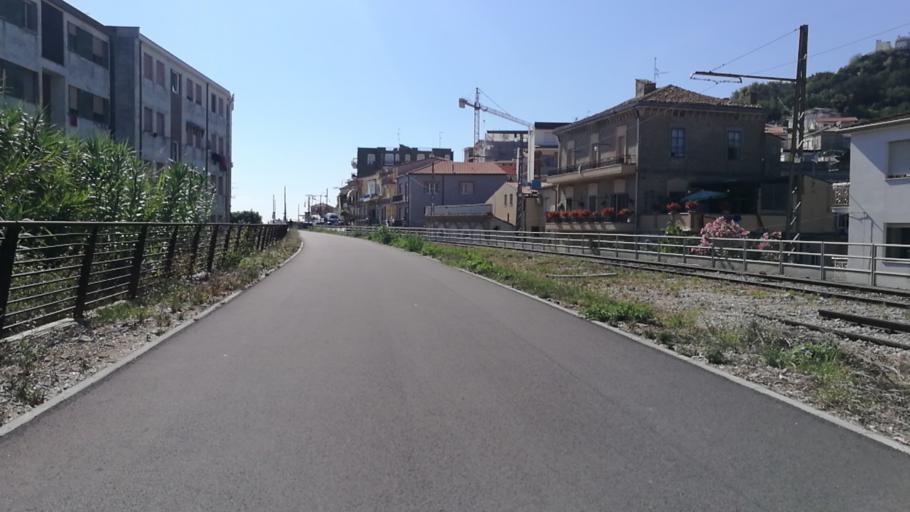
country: IT
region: Abruzzo
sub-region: Provincia di Chieti
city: Marina di San Vito
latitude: 42.3093
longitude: 14.4445
